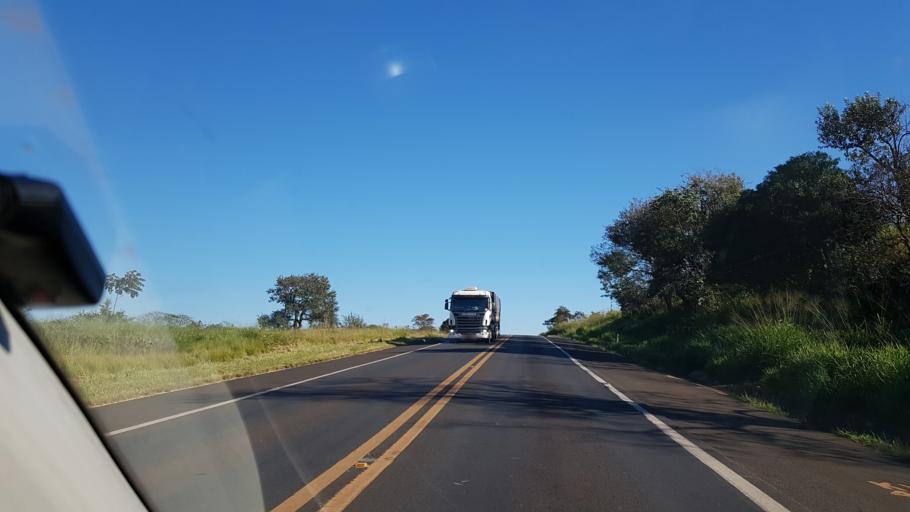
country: BR
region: Sao Paulo
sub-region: Assis
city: Assis
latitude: -22.6081
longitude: -50.4701
